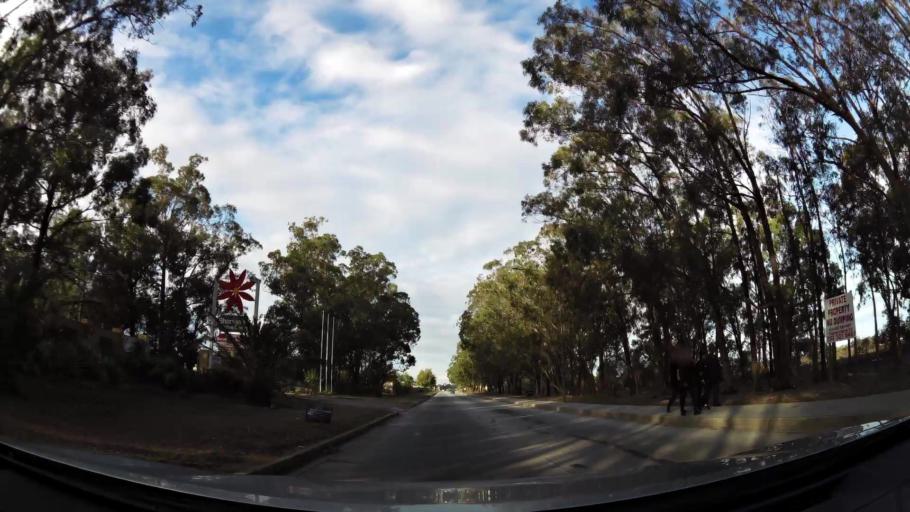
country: ZA
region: Eastern Cape
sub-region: Nelson Mandela Bay Metropolitan Municipality
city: Port Elizabeth
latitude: -33.9580
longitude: 25.4969
